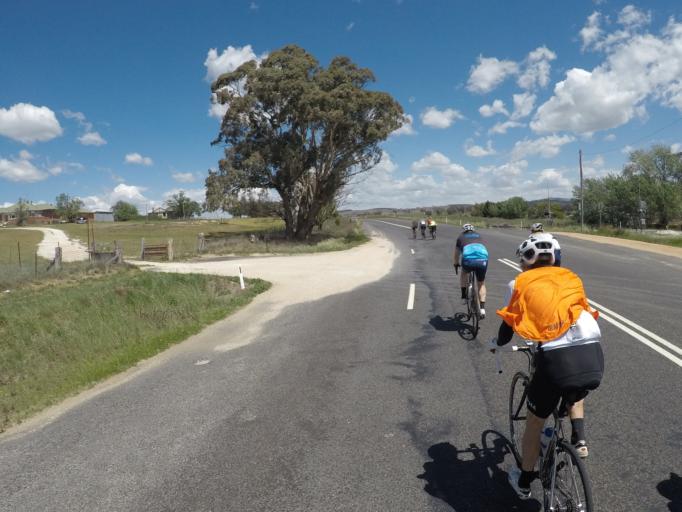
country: AU
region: New South Wales
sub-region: Bathurst Regional
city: Perthville
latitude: -33.5458
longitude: 149.4300
